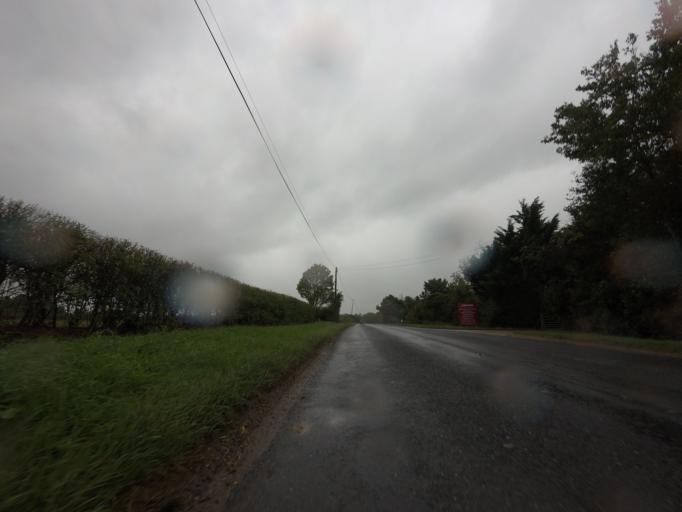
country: GB
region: England
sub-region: Cambridgeshire
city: Wimpole
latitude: 52.1843
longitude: -0.0561
